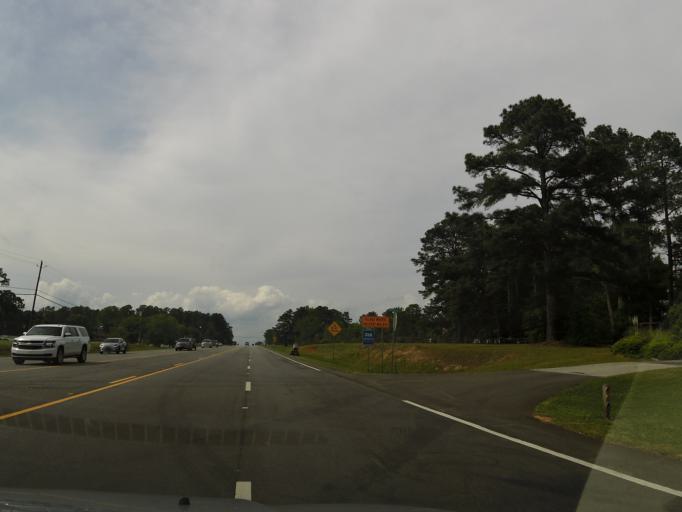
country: US
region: Georgia
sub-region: McDuffie County
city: Thomson
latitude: 33.5369
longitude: -82.5073
